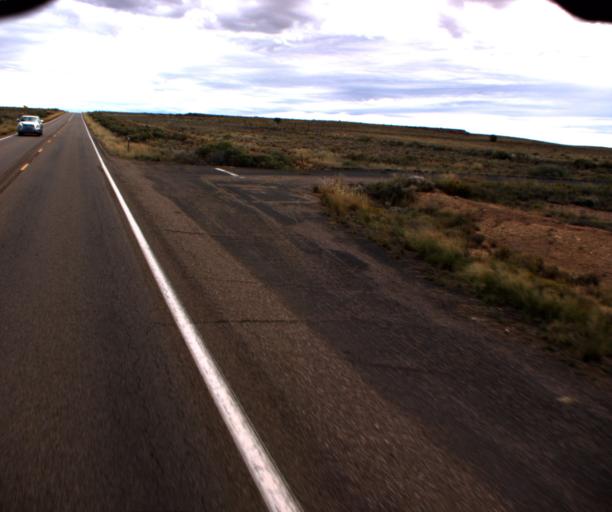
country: US
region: Arizona
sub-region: Navajo County
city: Holbrook
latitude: 34.8320
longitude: -110.1438
